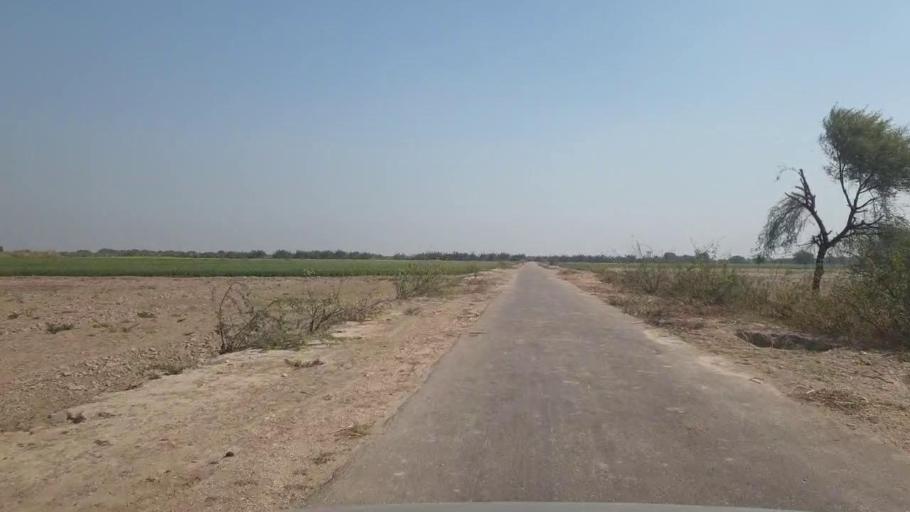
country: PK
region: Sindh
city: Chambar
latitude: 25.2395
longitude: 68.8488
